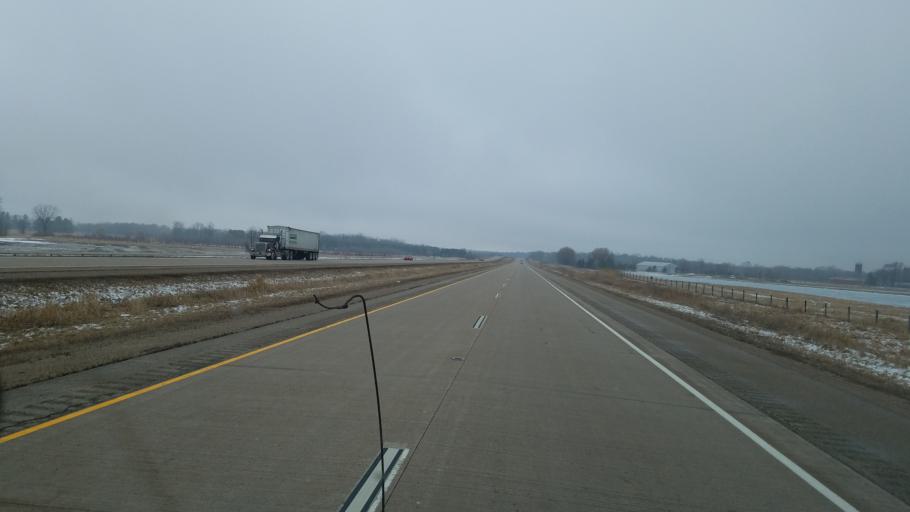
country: US
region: Wisconsin
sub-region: Winnebago County
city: Winneconne
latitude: 44.2389
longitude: -88.7870
